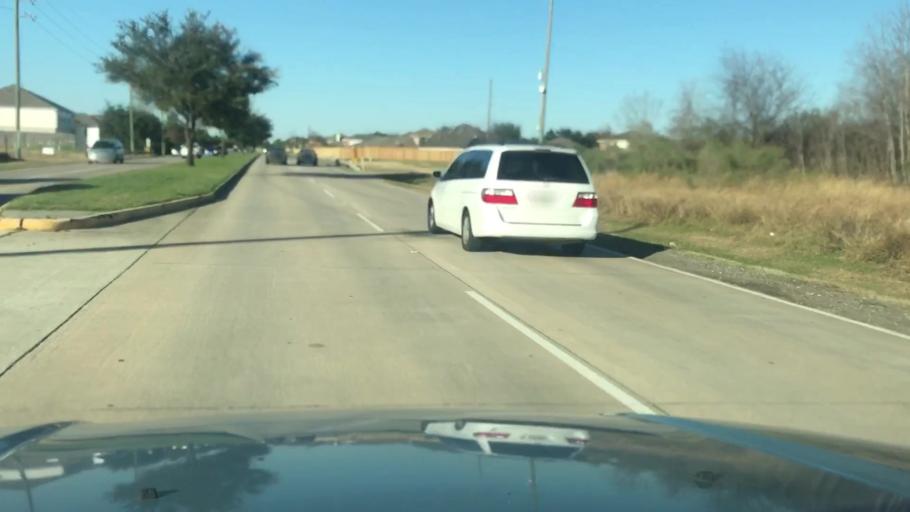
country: US
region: Texas
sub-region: Fort Bend County
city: Cinco Ranch
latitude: 29.8388
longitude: -95.7188
